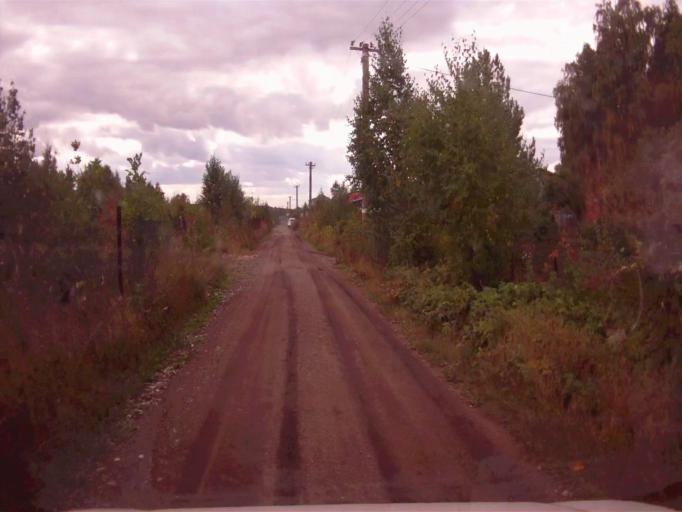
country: RU
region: Chelyabinsk
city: Sargazy
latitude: 55.1258
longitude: 61.2491
